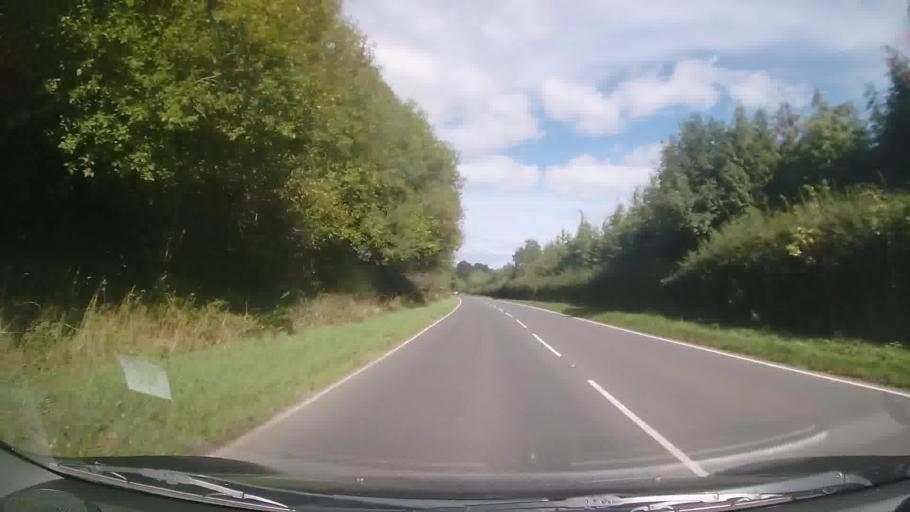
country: GB
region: England
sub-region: Herefordshire
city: Clifford
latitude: 52.1094
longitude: -3.1172
